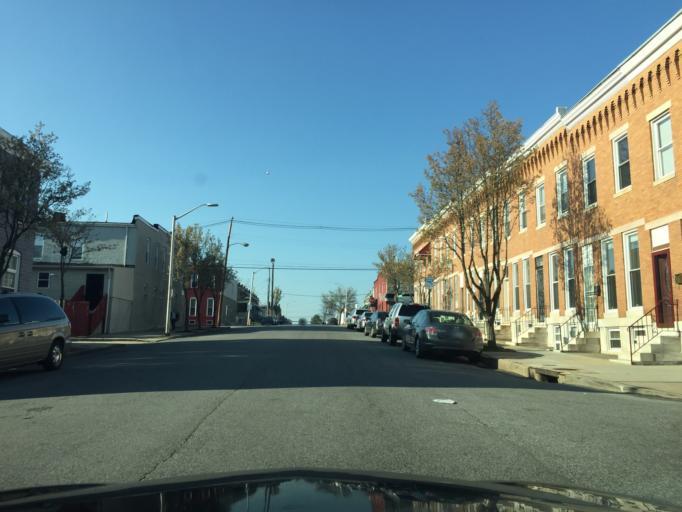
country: US
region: Maryland
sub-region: City of Baltimore
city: Baltimore
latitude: 39.3074
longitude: -76.5814
